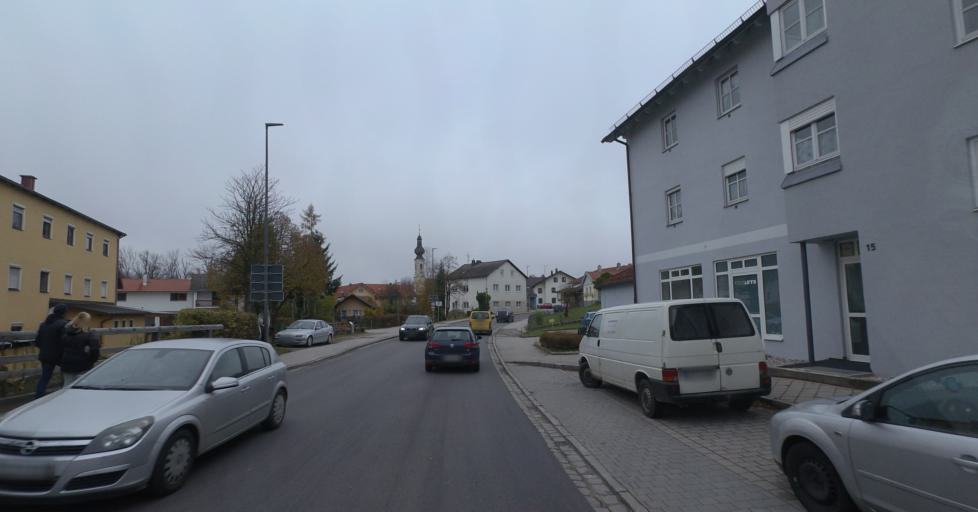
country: DE
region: Bavaria
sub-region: Upper Bavaria
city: Trostberg an der Alz
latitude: 48.0012
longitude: 12.5347
